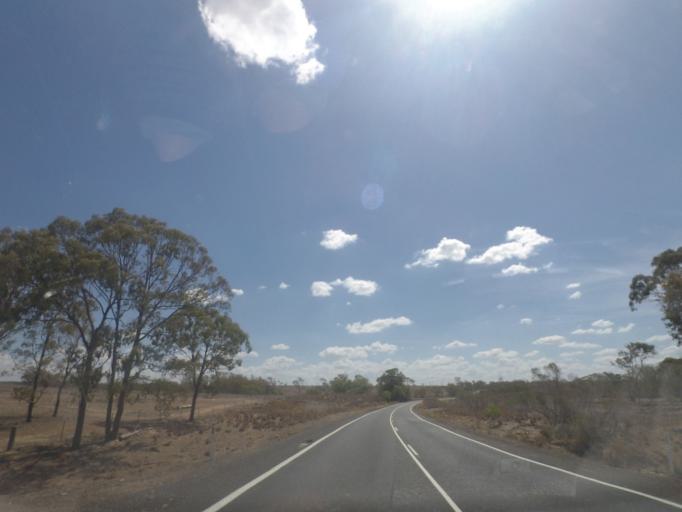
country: AU
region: Queensland
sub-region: Southern Downs
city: Warwick
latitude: -28.2056
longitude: 151.5838
